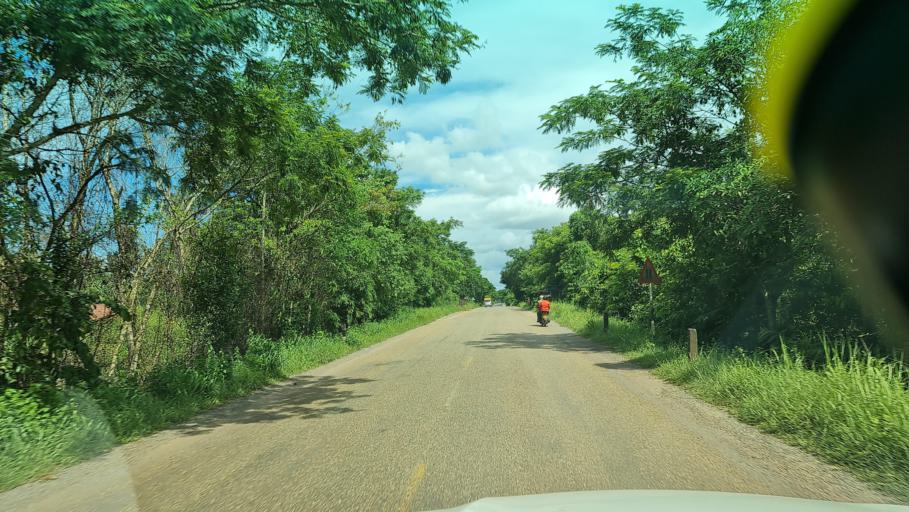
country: LA
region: Bolikhamxai
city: Ban Nahin
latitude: 18.2282
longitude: 104.1943
